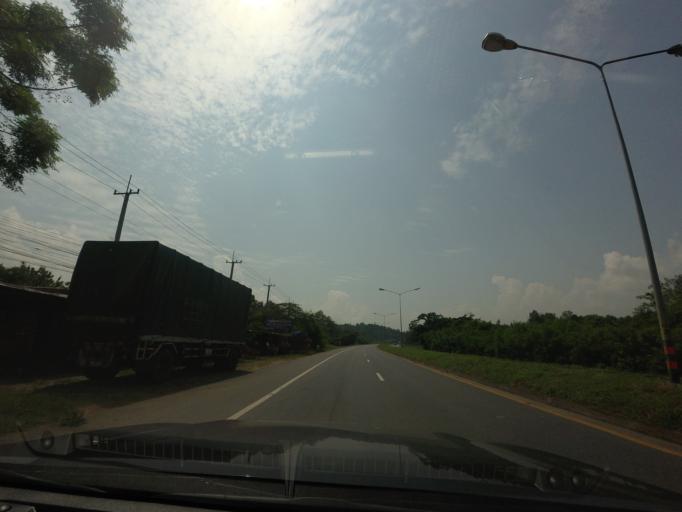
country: TH
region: Phrae
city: Den Chai
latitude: 17.9525
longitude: 100.0684
